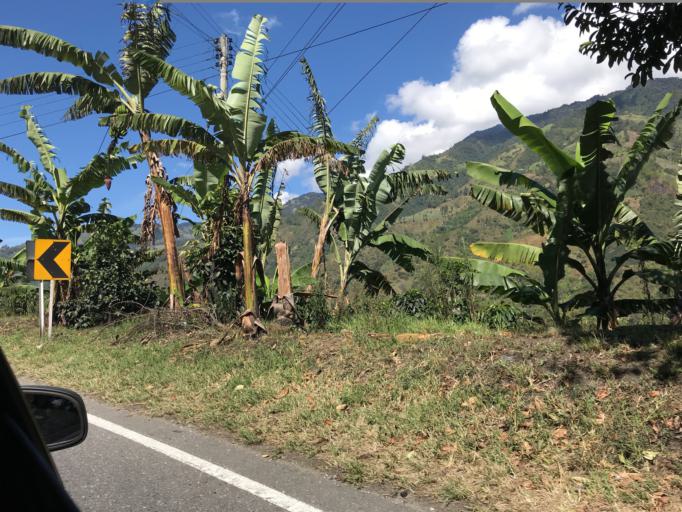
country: CO
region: Tolima
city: Cajamarca
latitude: 4.4433
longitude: -75.4110
